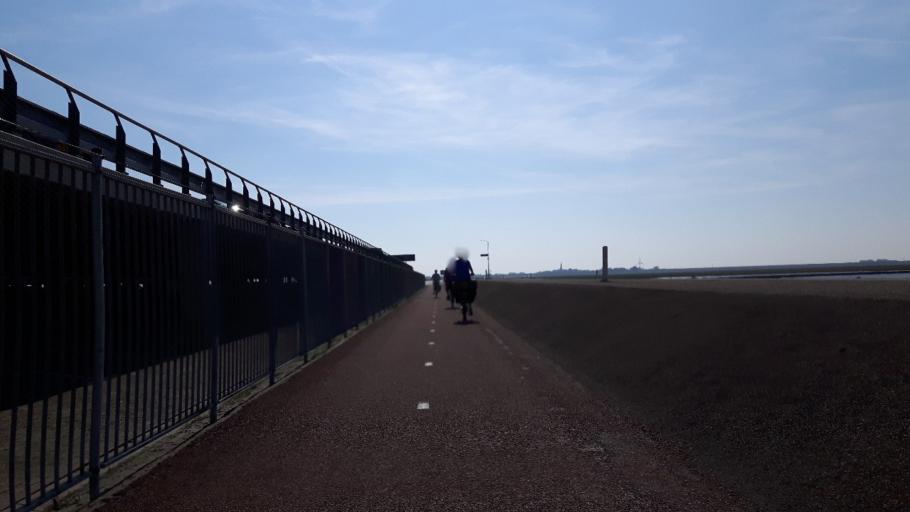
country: NL
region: Friesland
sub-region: Gemeente Dongeradeel
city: Holwerd
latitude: 53.3929
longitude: 5.8814
